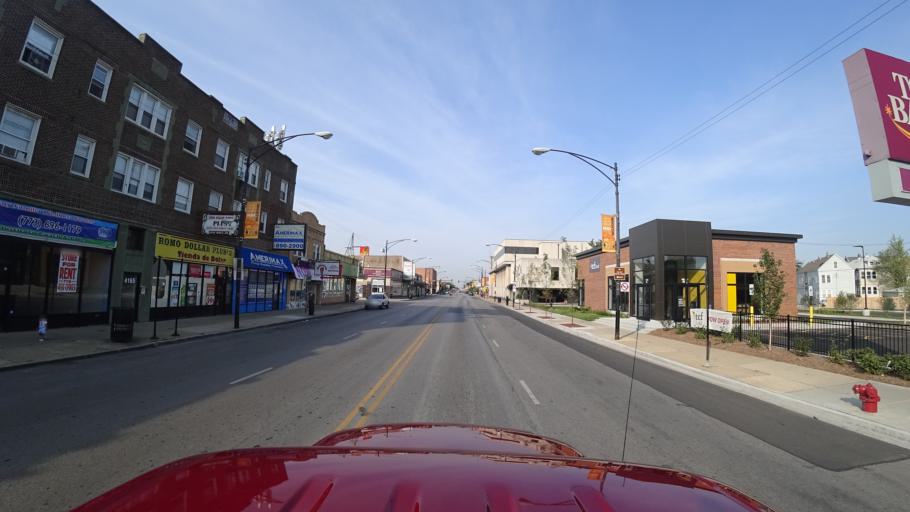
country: US
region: Illinois
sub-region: Cook County
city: Chicago
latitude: 41.8180
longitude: -87.6980
